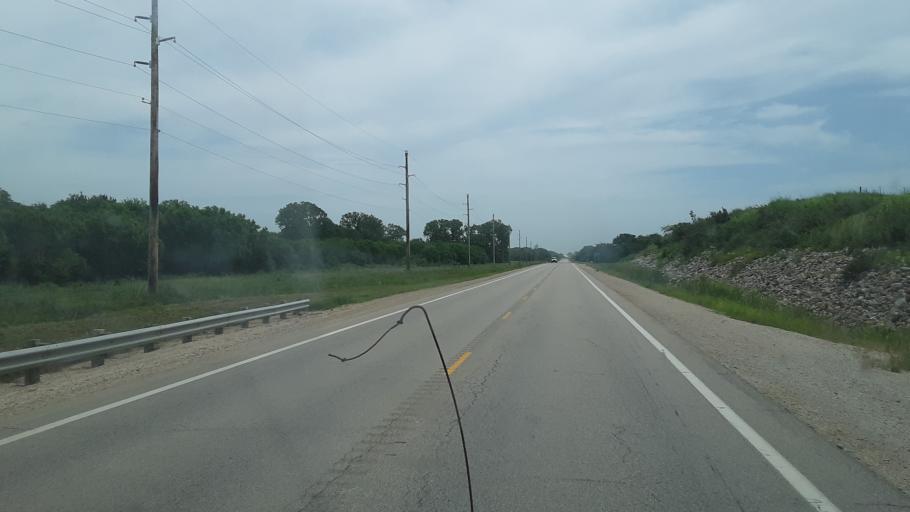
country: US
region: Kansas
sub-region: Woodson County
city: Yates Center
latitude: 37.8369
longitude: -95.9949
